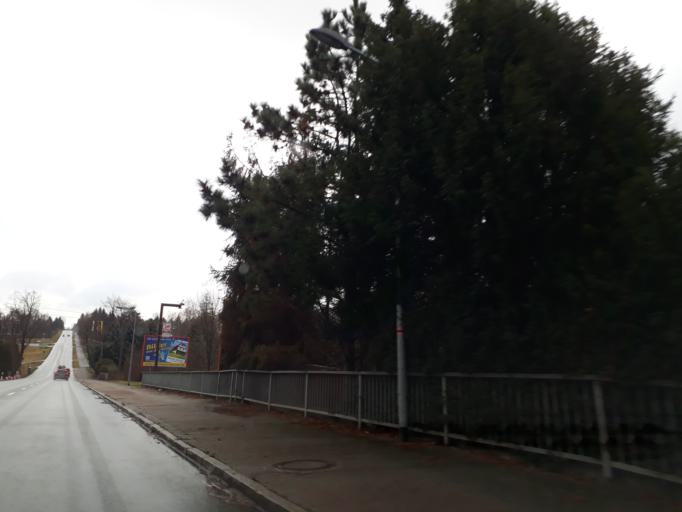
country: DE
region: Saxony
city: Herrnhut
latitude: 51.0283
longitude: 14.7235
